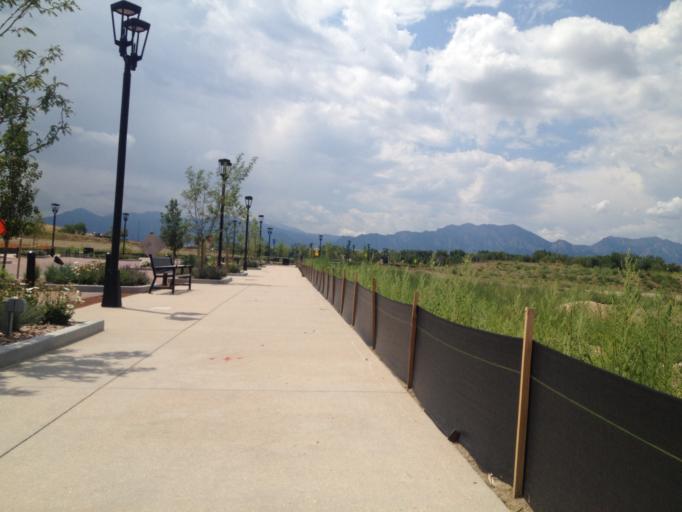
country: US
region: Colorado
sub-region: Boulder County
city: Superior
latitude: 39.9519
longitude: -105.1612
